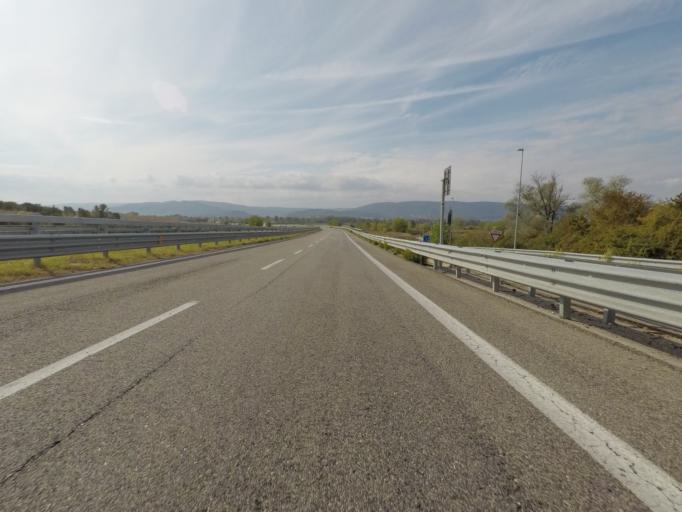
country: IT
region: Tuscany
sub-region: Provincia di Siena
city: Rosia
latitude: 43.2428
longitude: 11.2843
